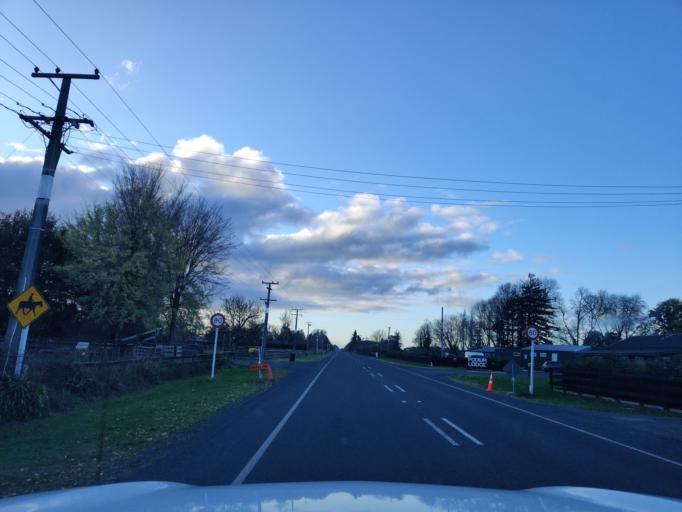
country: NZ
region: Waikato
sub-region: Waipa District
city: Cambridge
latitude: -37.8869
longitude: 175.4388
